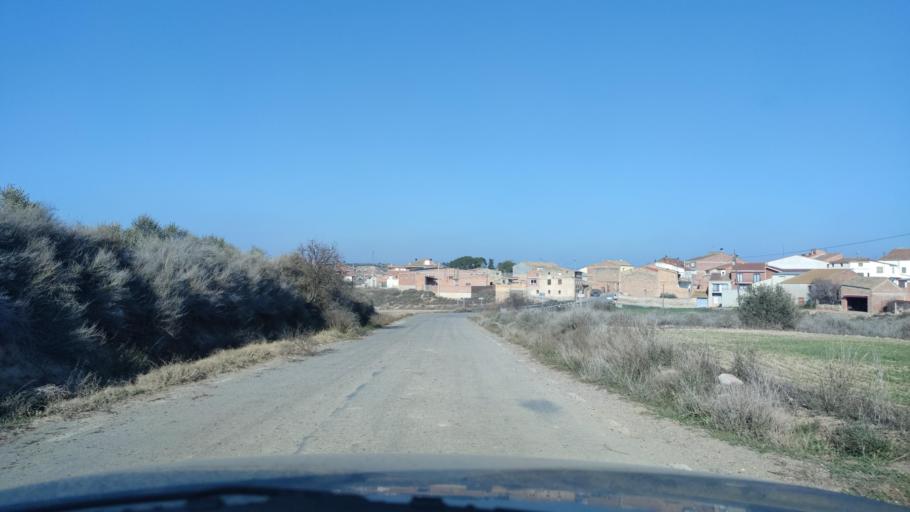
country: ES
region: Catalonia
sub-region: Provincia de Lleida
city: Torrebesses
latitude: 41.4575
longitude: 0.5588
